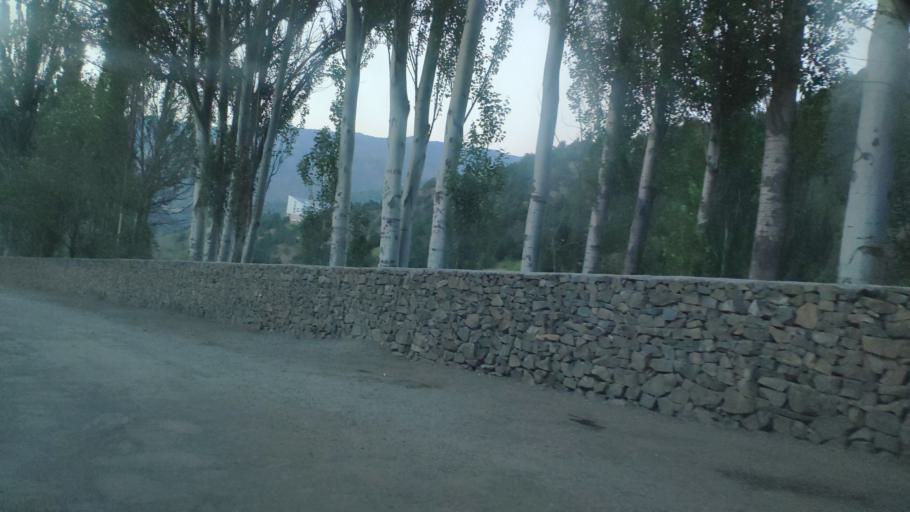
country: TJ
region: Viloyati Sughd
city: Ayni
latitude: 39.6292
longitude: 68.4929
